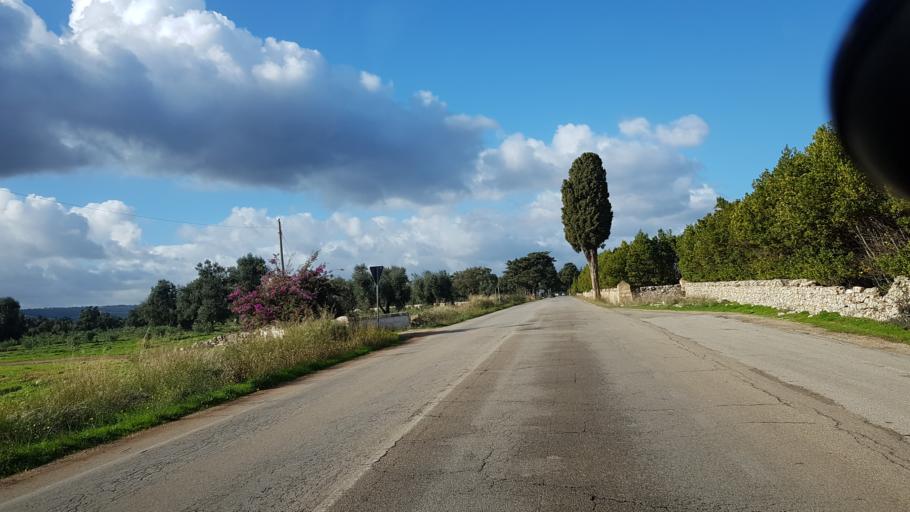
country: IT
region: Apulia
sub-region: Provincia di Brindisi
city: Pezze di Greco
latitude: 40.7995
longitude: 17.4424
